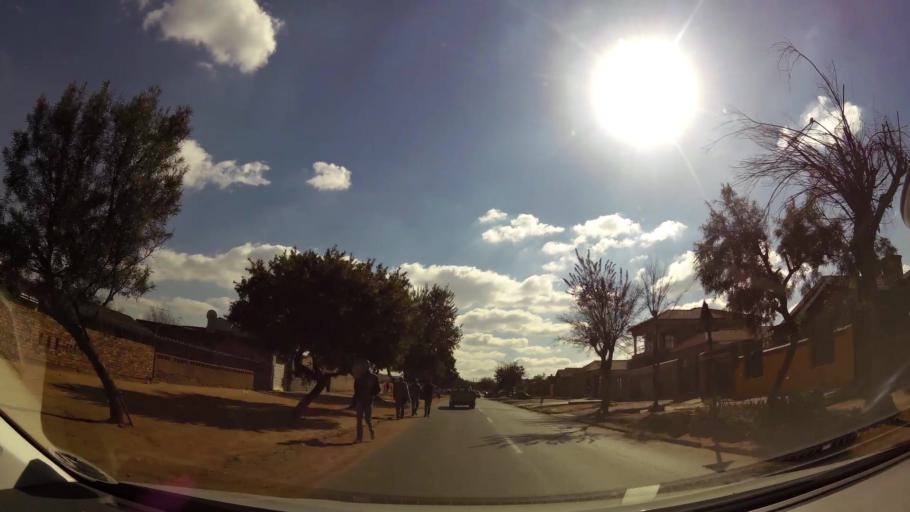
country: ZA
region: Gauteng
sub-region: City of Johannesburg Metropolitan Municipality
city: Soweto
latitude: -26.2172
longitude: 27.8804
